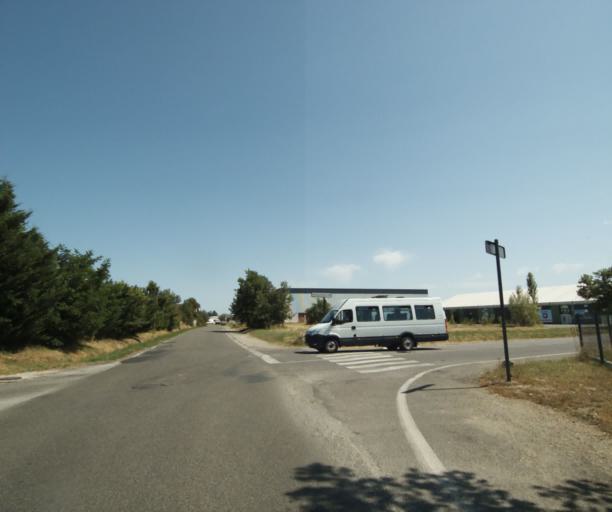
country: FR
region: Midi-Pyrenees
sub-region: Departement du Tarn-et-Garonne
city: Montauban
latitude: 44.0398
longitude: 1.3718
